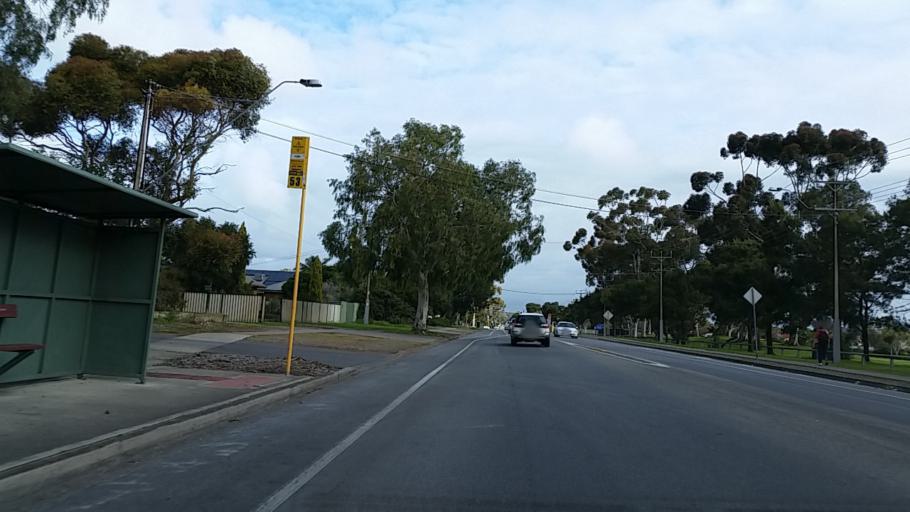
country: AU
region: South Australia
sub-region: Onkaparinga
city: Morphett Vale
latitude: -35.1269
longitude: 138.5365
